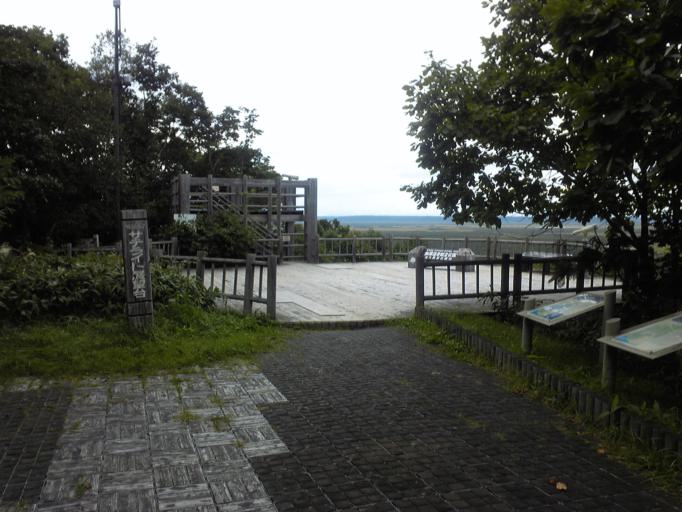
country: JP
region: Hokkaido
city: Kushiro
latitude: 43.0742
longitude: 144.3199
